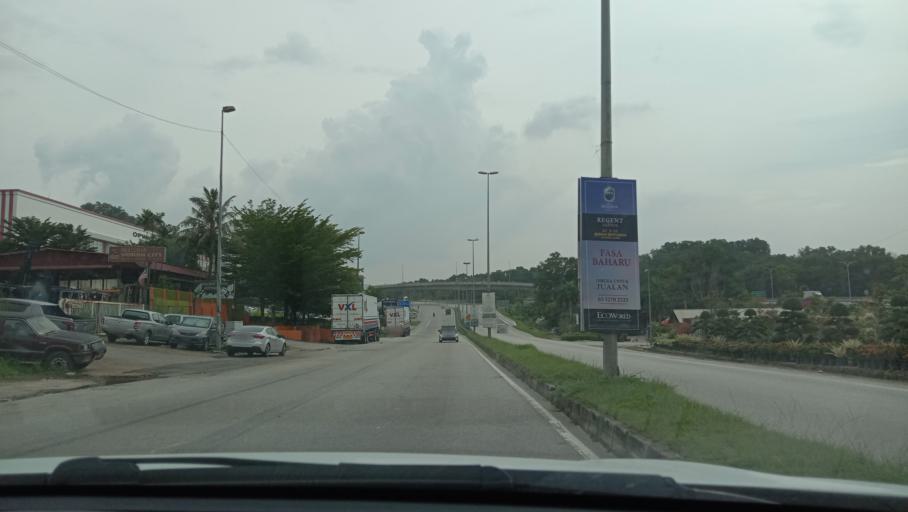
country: MY
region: Selangor
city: Kampung Baru Subang
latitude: 3.1318
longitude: 101.5259
